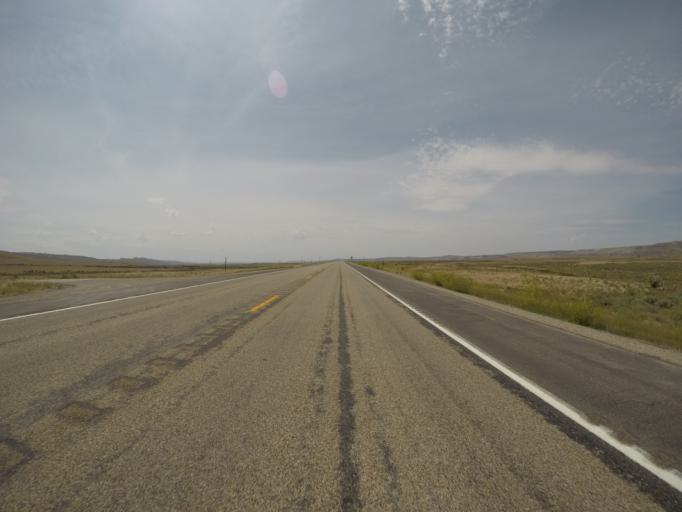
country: US
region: Wyoming
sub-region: Lincoln County
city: Kemmerer
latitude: 41.7355
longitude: -110.5642
